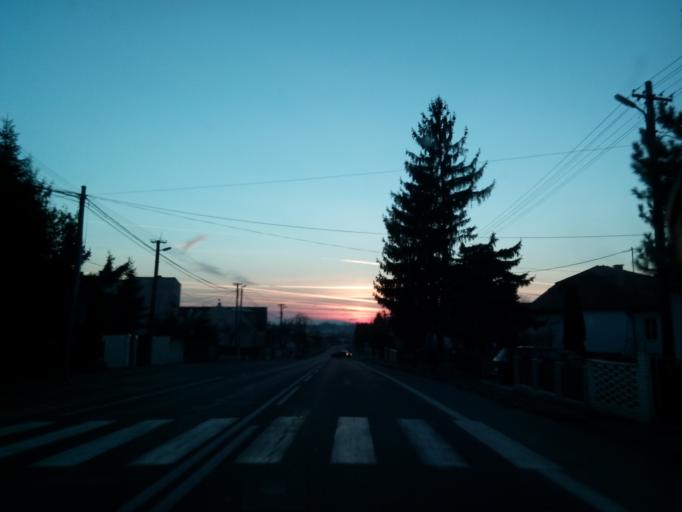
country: SK
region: Kosicky
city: Vinne
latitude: 48.7665
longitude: 22.0711
